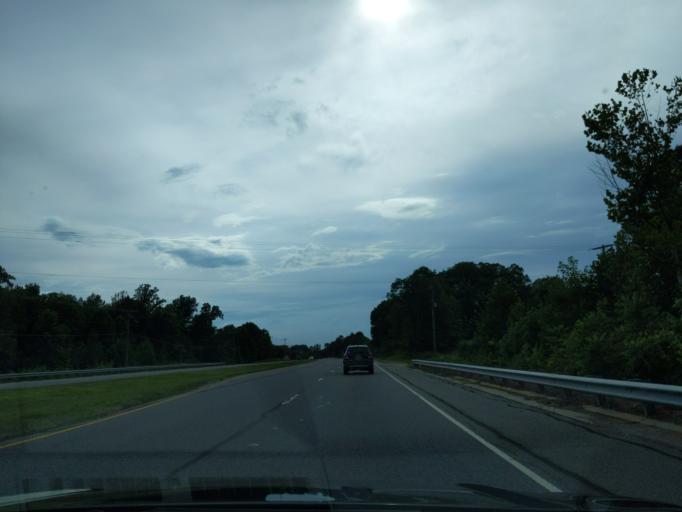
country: US
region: North Carolina
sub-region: Cabarrus County
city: Concord
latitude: 35.3855
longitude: -80.5168
